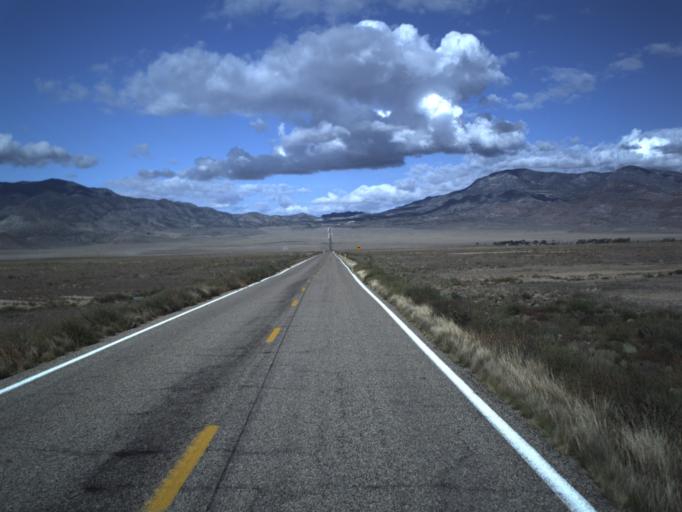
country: US
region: Utah
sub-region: Beaver County
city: Milford
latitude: 38.4681
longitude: -113.3997
